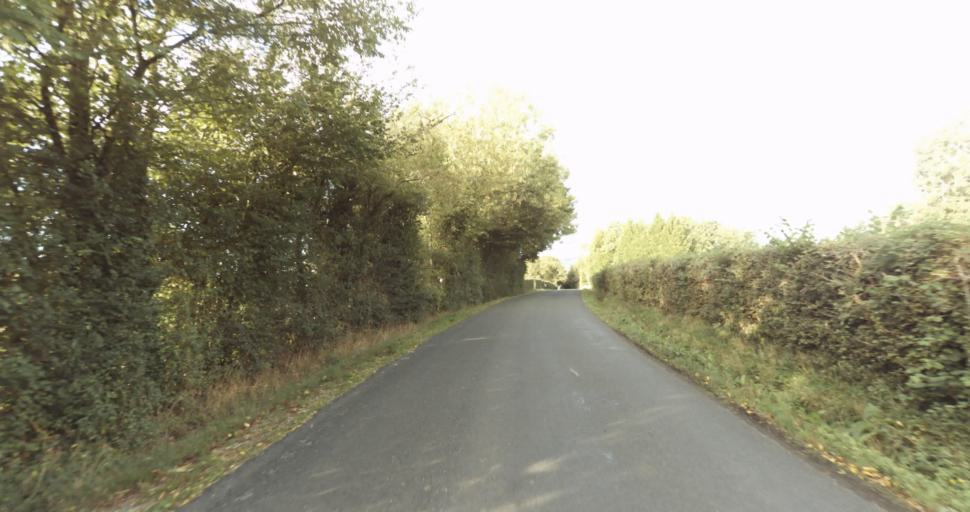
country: FR
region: Lower Normandy
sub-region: Departement de l'Orne
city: Vimoutiers
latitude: 48.8811
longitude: 0.2375
